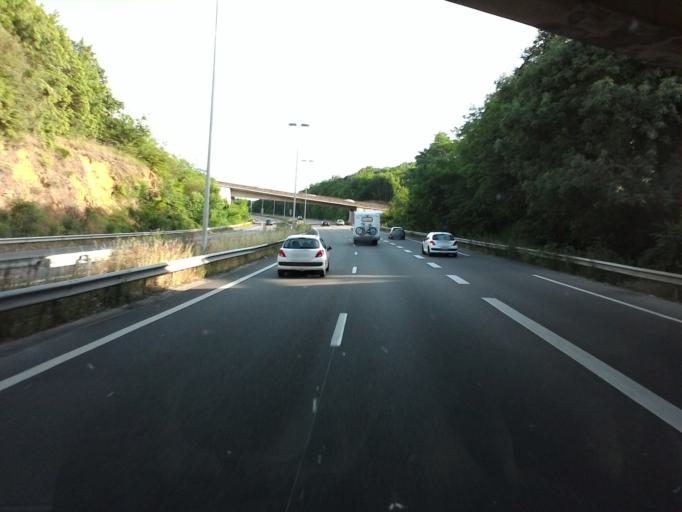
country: FR
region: Lorraine
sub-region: Departement de Meurthe-et-Moselle
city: Laxou
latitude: 48.6957
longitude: 6.1168
